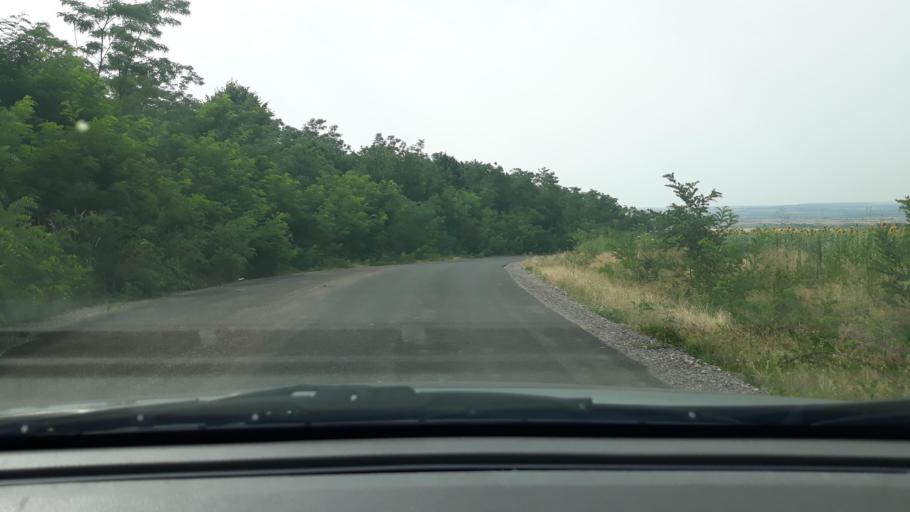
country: RO
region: Bihor
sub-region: Comuna Chislaz
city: Misca
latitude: 47.2617
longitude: 22.2926
